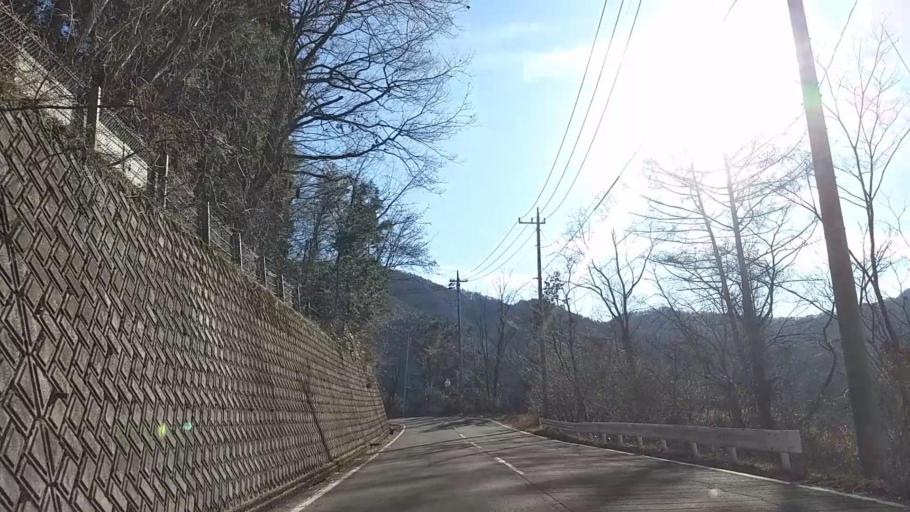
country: JP
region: Yamanashi
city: Otsuki
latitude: 35.5127
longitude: 138.9576
